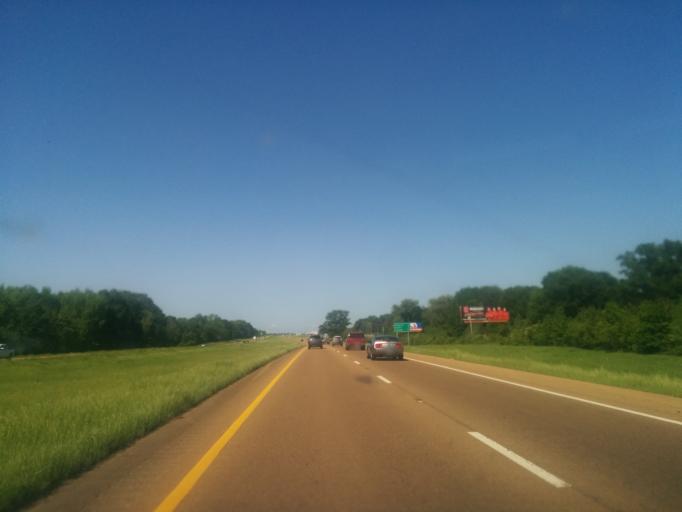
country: US
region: Mississippi
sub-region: Madison County
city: Canton
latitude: 32.5517
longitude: -90.0877
